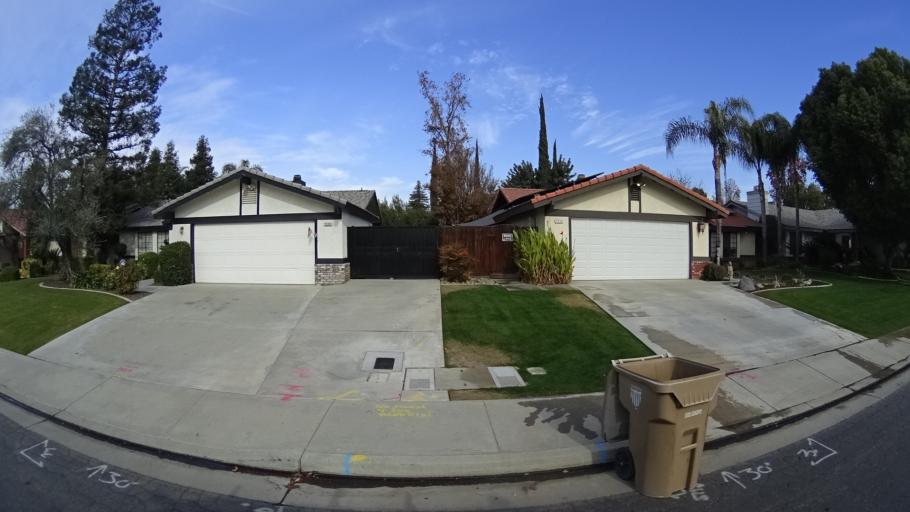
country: US
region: California
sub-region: Kern County
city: Greenacres
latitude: 35.4030
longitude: -119.0818
